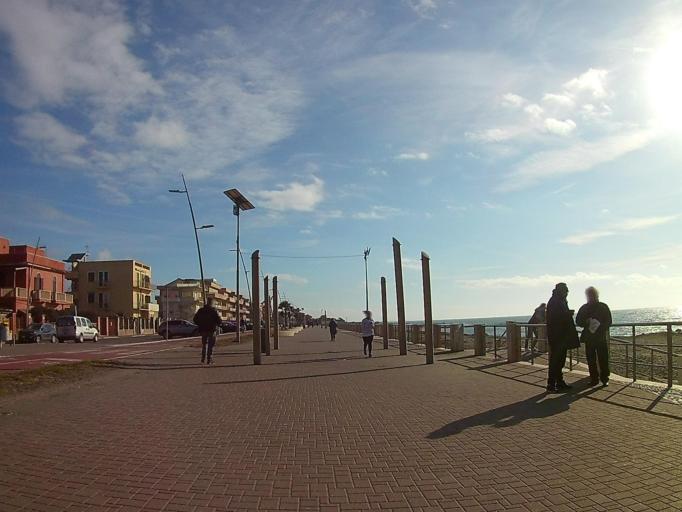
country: IT
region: Latium
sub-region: Citta metropolitana di Roma Capitale
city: Lido di Ostia
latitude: 41.7346
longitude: 12.2611
